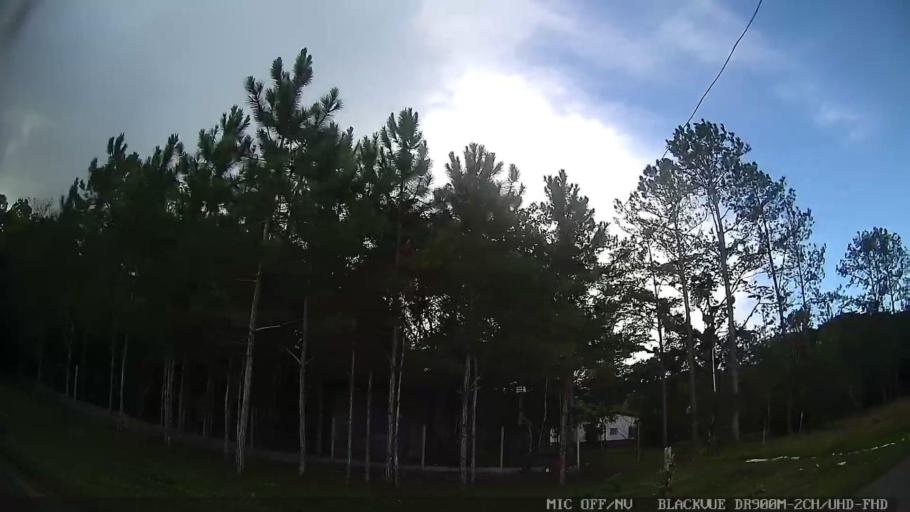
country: BR
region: Sao Paulo
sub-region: Peruibe
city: Peruibe
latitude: -24.1986
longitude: -46.9395
